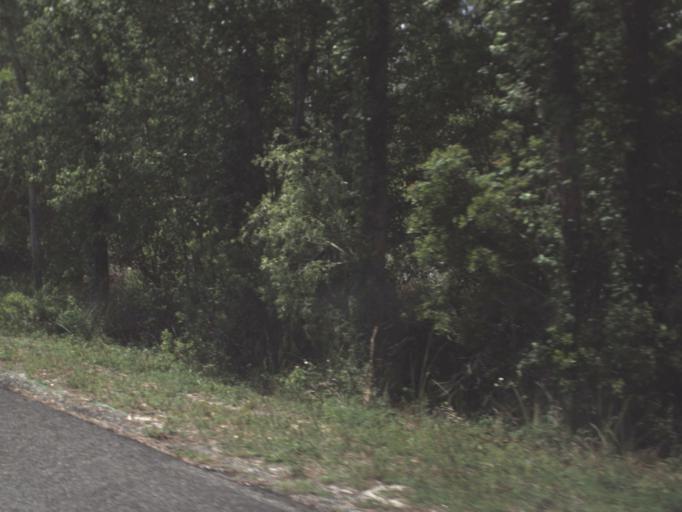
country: US
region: Florida
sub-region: Flagler County
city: Bunnell
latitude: 29.4373
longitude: -81.2349
